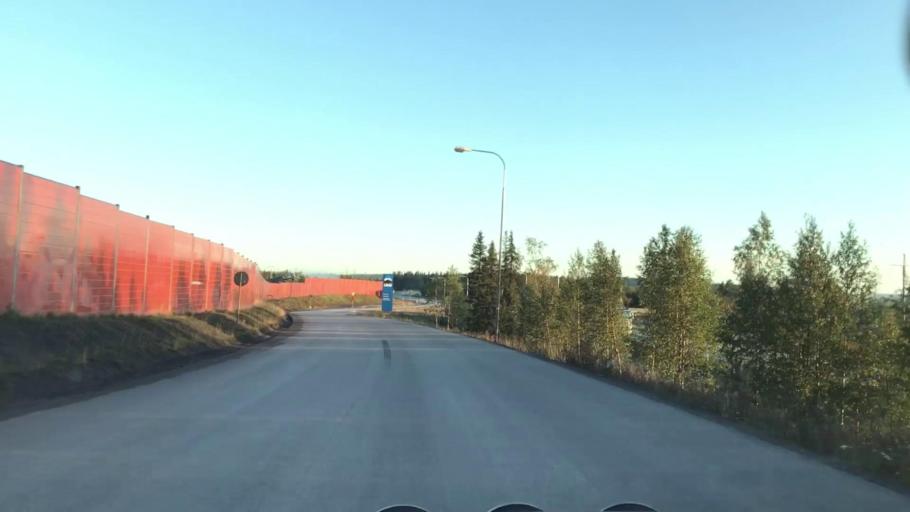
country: SE
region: Norrbotten
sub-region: Gallivare Kommun
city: Malmberget
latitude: 67.6510
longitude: 21.0176
